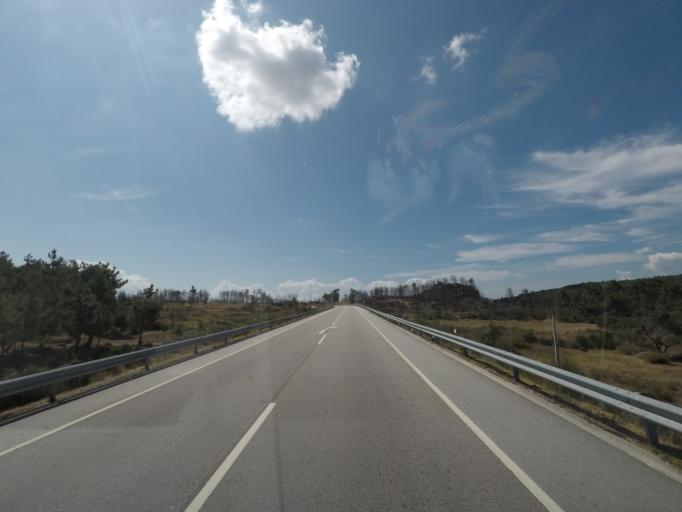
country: PT
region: Vila Real
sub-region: Murca
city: Murca
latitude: 41.3318
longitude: -7.4714
